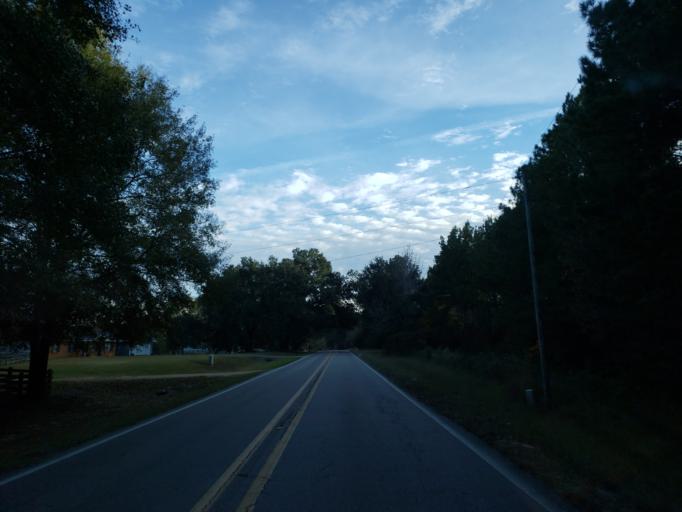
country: US
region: Mississippi
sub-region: Lamar County
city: Purvis
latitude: 31.1775
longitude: -89.4335
